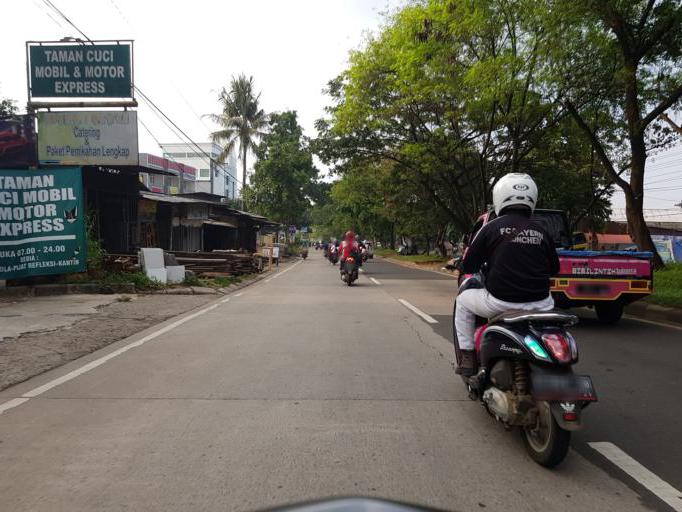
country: ID
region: West Java
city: Bogor
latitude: -6.5470
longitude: 106.7741
